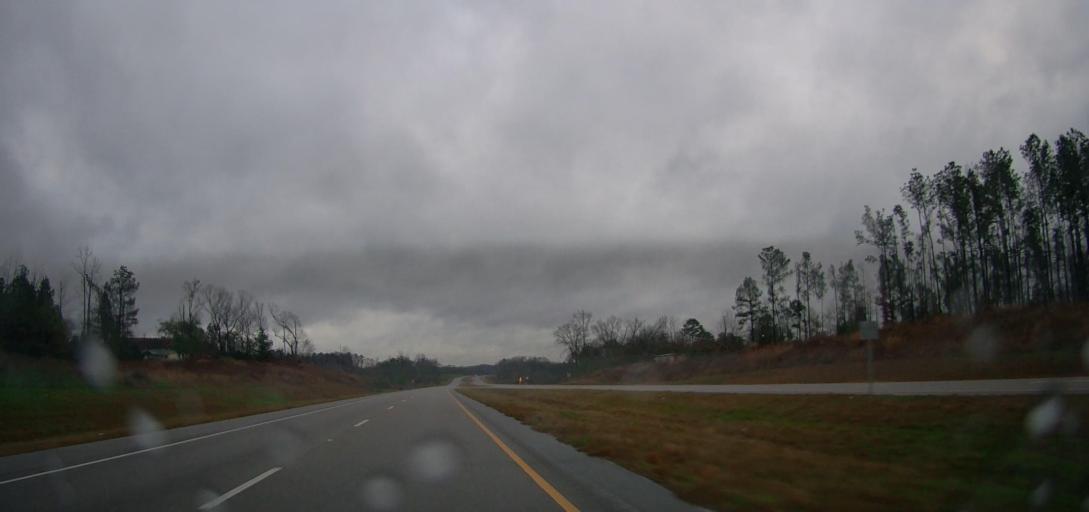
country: US
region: Alabama
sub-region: Bibb County
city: Centreville
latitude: 32.9425
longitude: -87.0786
